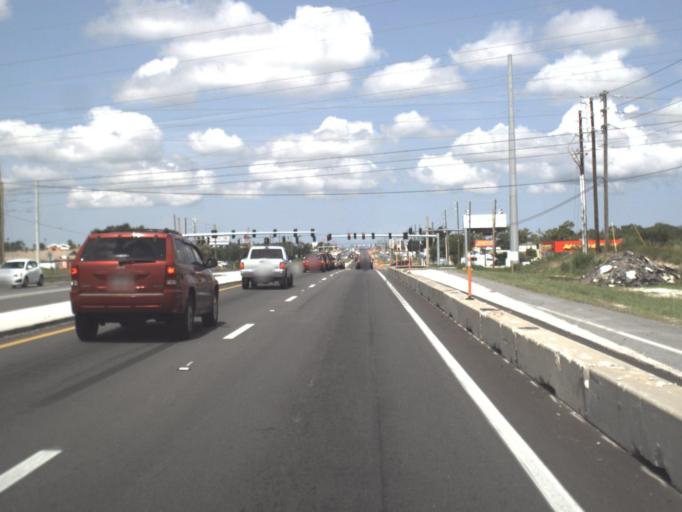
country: US
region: Florida
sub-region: Hernando County
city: Brookridge
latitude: 28.5338
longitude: -82.4979
